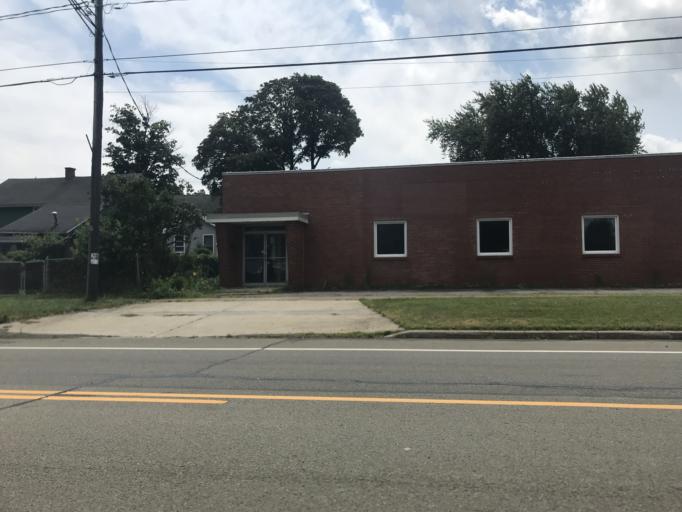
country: US
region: New York
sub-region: Chautauqua County
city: Dunkirk
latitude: 42.4865
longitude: -79.3407
